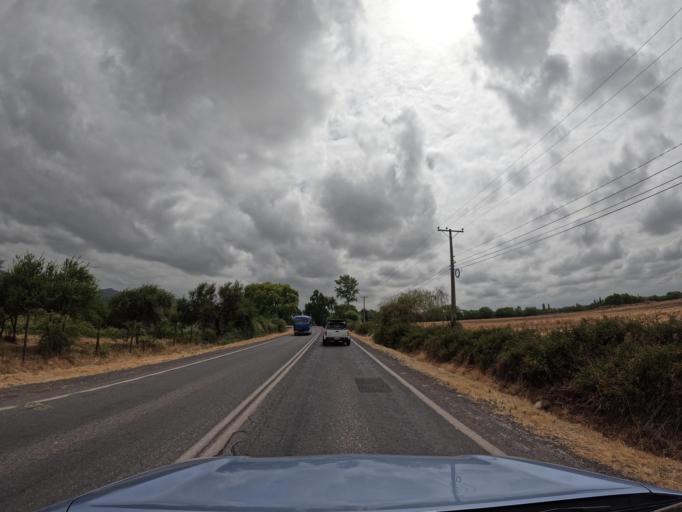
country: CL
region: Maule
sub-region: Provincia de Curico
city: Teno
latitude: -34.8460
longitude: -71.1875
